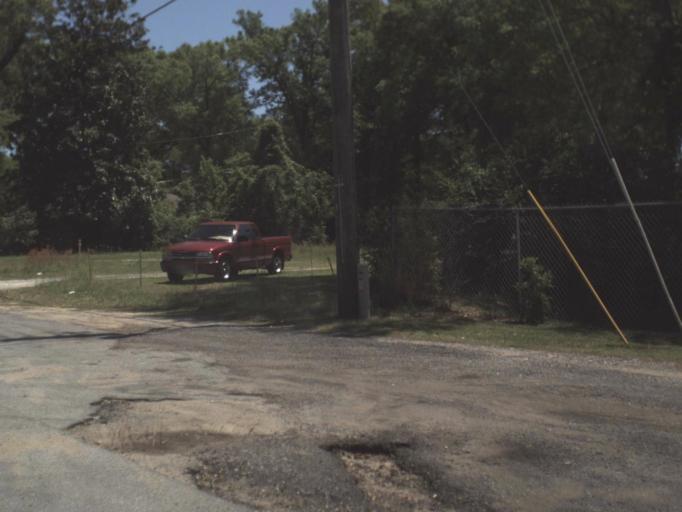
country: US
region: Florida
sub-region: Escambia County
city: Bellview
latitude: 30.4867
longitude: -87.3058
